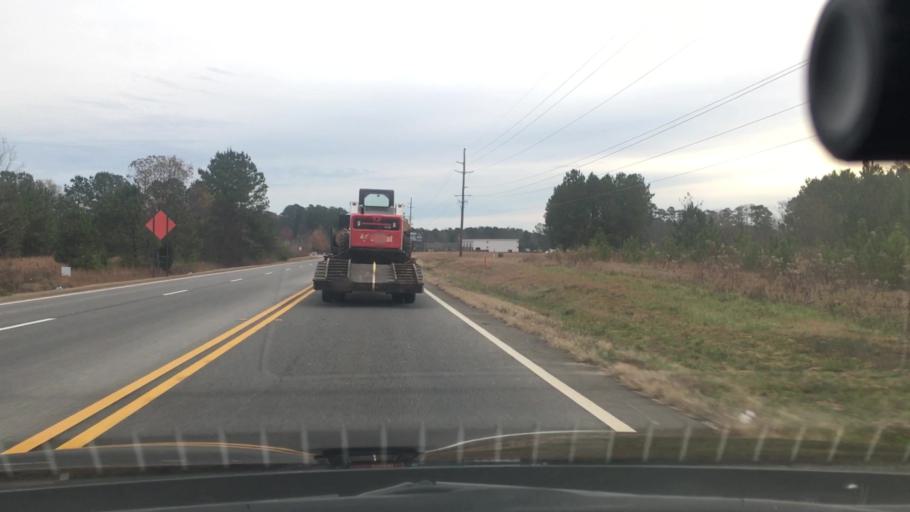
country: US
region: Georgia
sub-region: Coweta County
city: Senoia
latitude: 33.2933
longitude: -84.5771
